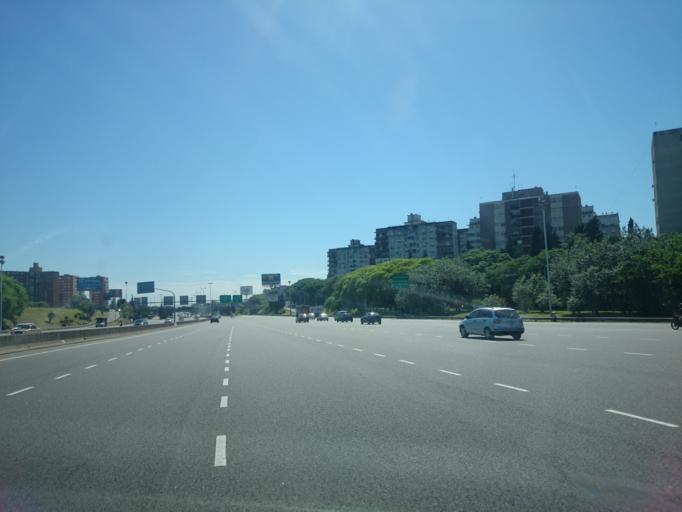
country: AR
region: Buenos Aires F.D.
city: Villa Lugano
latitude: -34.6975
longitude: -58.4944
